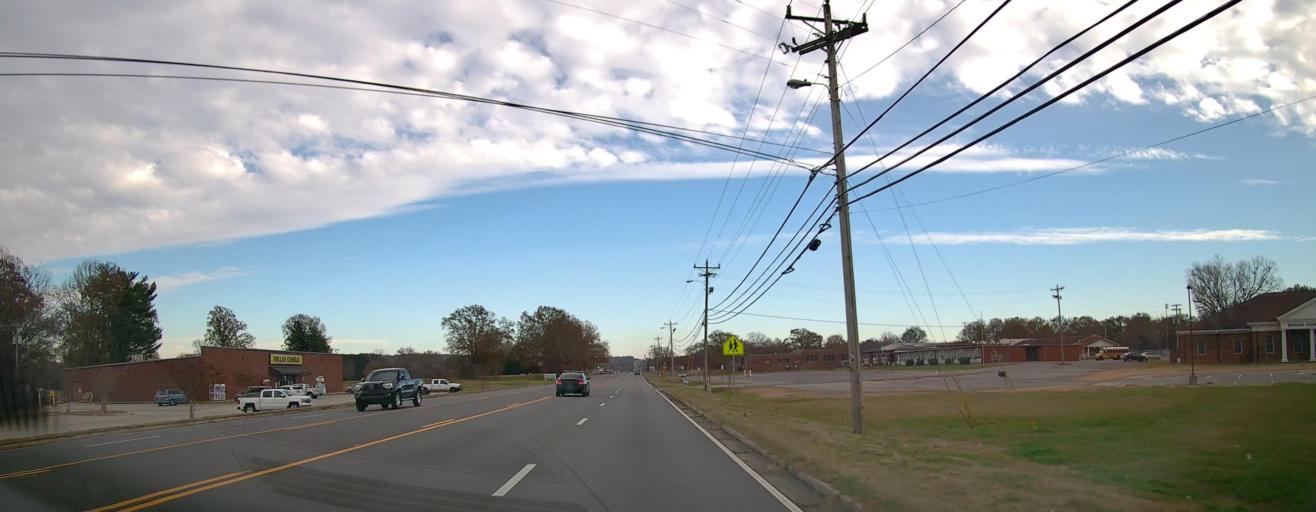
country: US
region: Alabama
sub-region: Morgan County
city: Priceville
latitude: 34.5293
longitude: -86.9004
